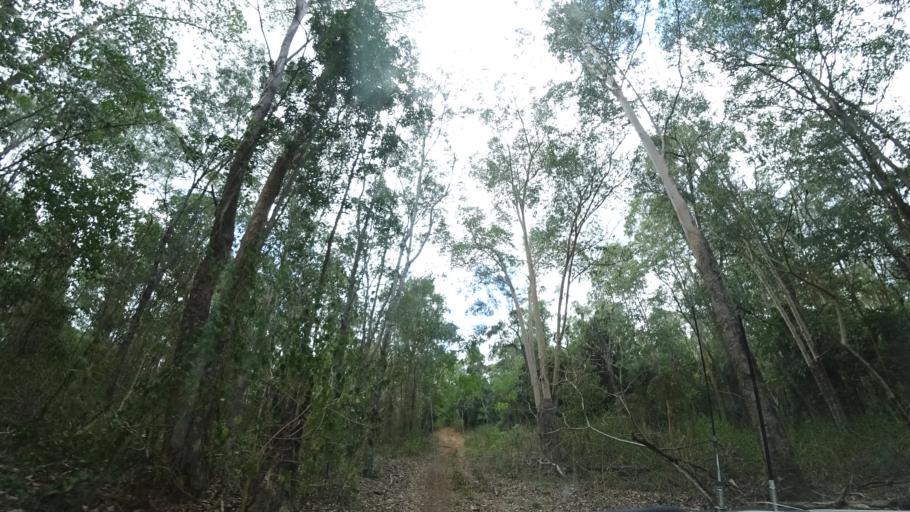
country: AU
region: Queensland
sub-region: Moreton Bay
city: Highvale
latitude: -27.4161
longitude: 152.7345
